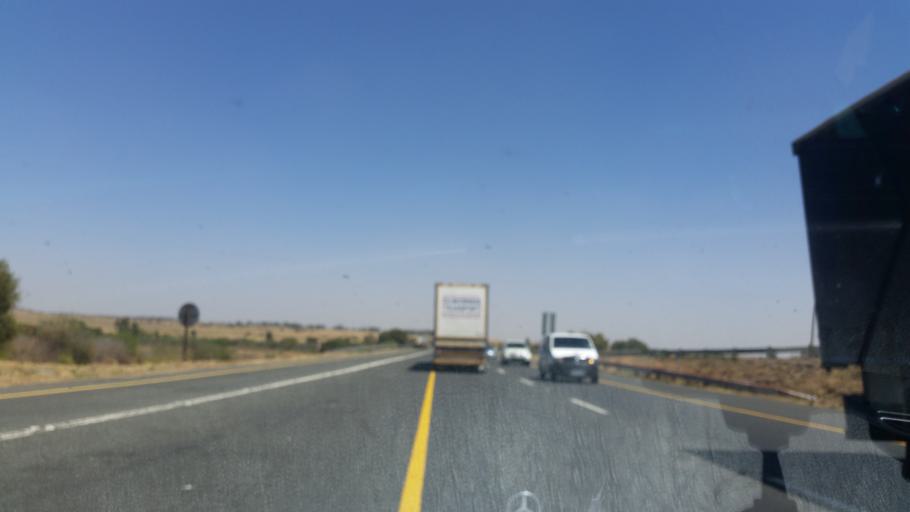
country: ZA
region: Orange Free State
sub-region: Lejweleputswa District Municipality
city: Winburg
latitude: -28.6290
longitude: 26.9076
